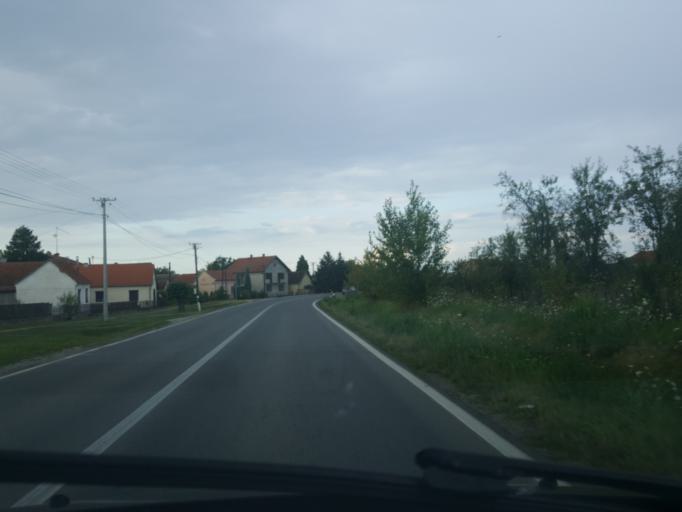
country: RS
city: Zminjak
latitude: 44.7291
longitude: 19.4530
